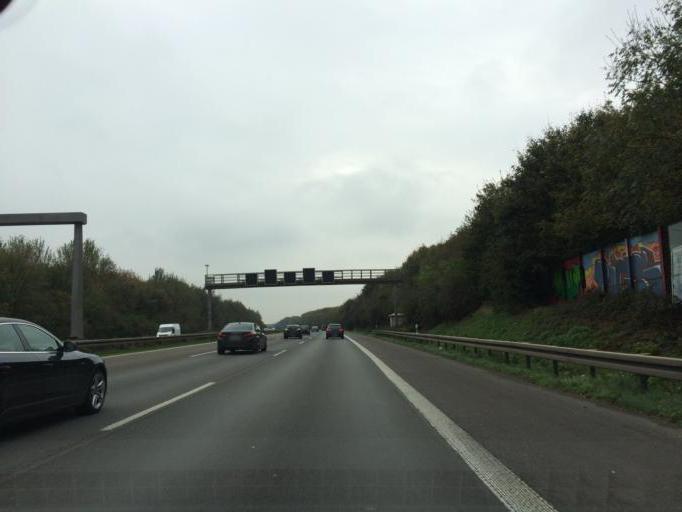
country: DE
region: North Rhine-Westphalia
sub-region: Regierungsbezirk Koln
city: Bilderstoeckchen
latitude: 51.0150
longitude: 6.9219
